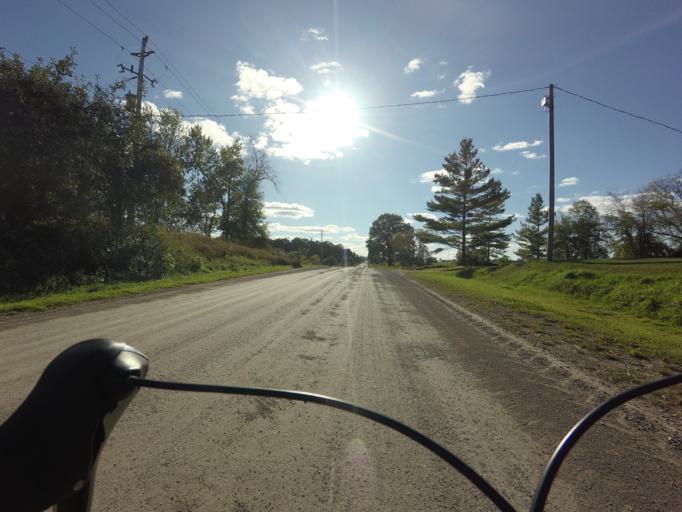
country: CA
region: Ontario
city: Bells Corners
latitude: 45.1227
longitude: -75.6854
